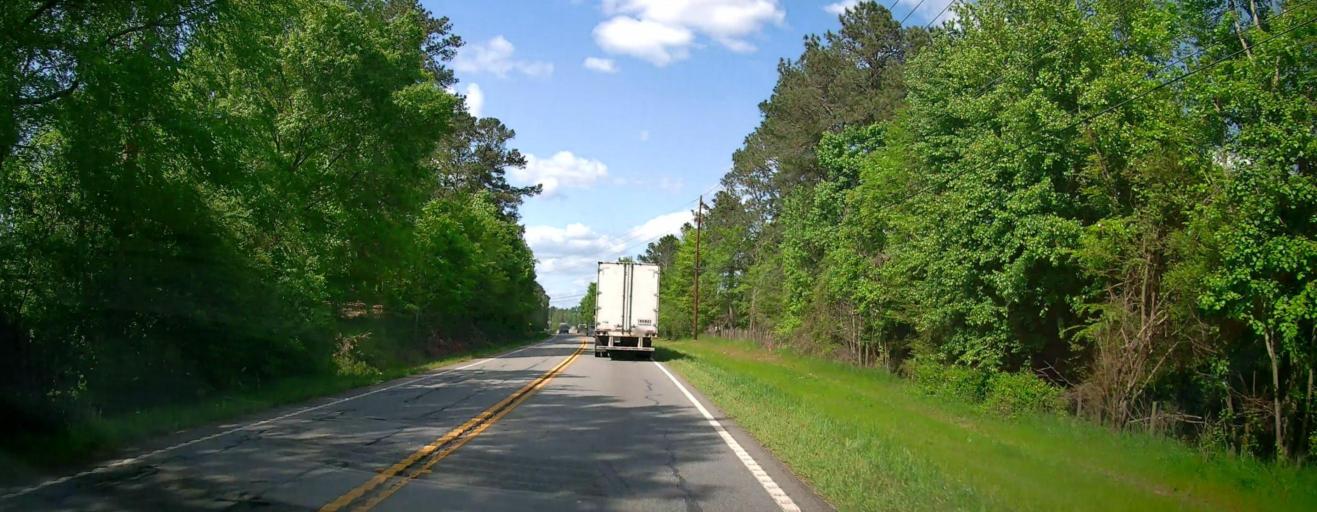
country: US
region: Georgia
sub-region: Greene County
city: Greensboro
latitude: 33.5256
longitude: -83.2211
